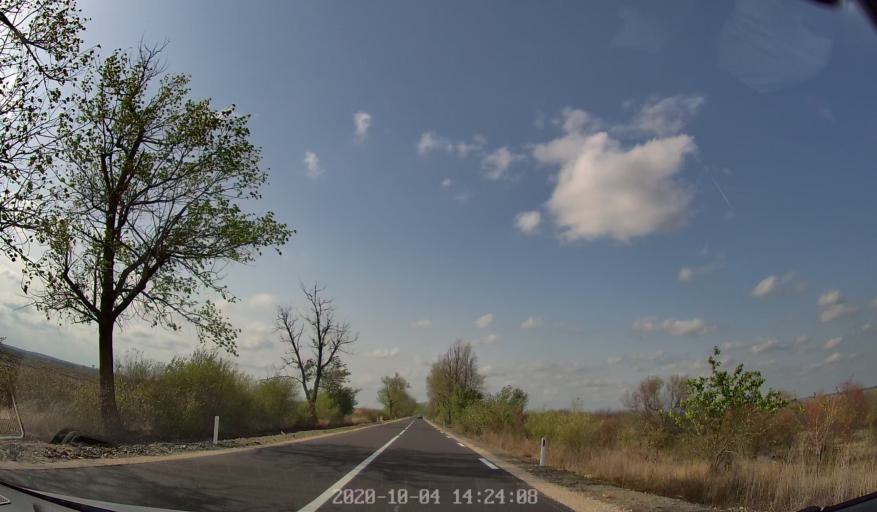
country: MD
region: Rezina
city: Saharna
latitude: 47.6131
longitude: 28.9232
